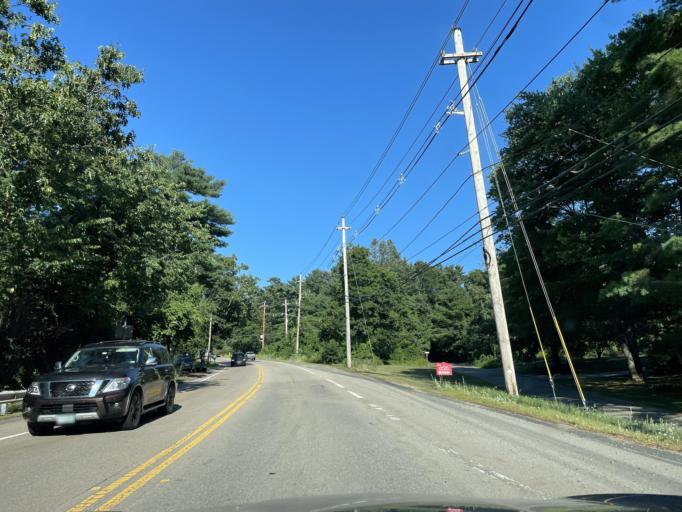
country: US
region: Massachusetts
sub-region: Norfolk County
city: Wrentham
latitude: 42.0727
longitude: -71.3475
